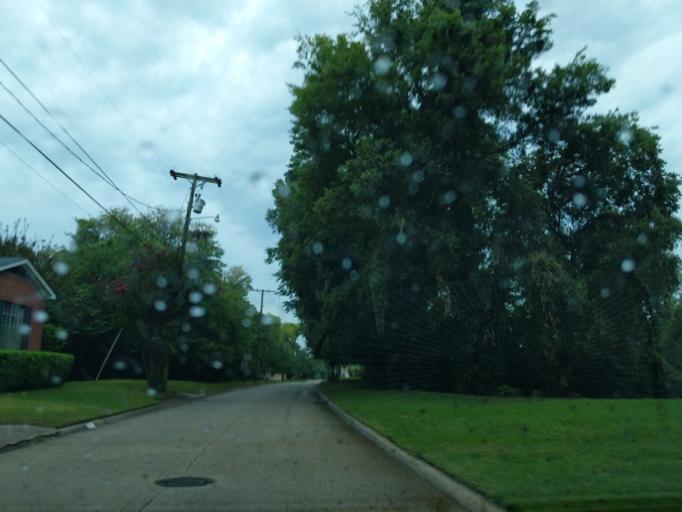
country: US
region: Mississippi
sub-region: Warren County
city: Vicksburg
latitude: 32.3622
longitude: -90.8745
